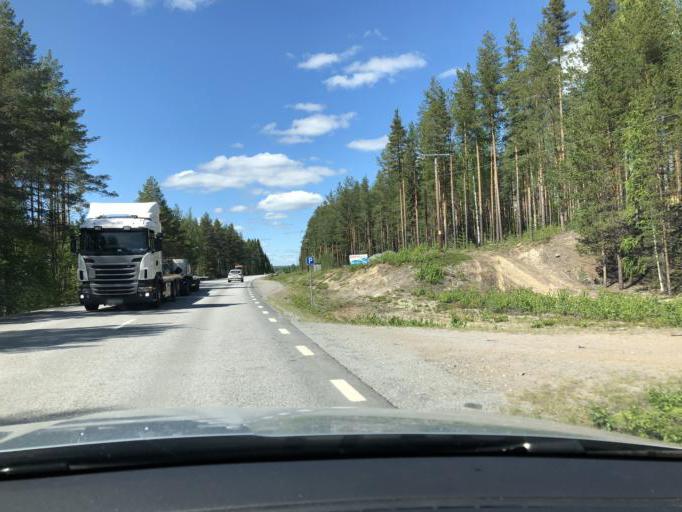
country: SE
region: Norrbotten
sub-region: Alvsbyns Kommun
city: AElvsbyn
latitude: 65.6509
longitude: 21.0829
